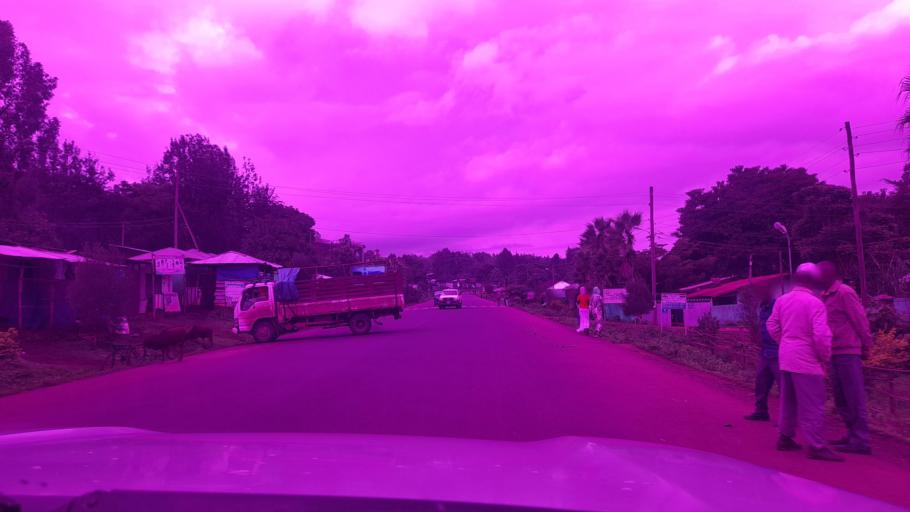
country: ET
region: Oromiya
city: Jima
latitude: 7.9267
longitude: 37.4201
